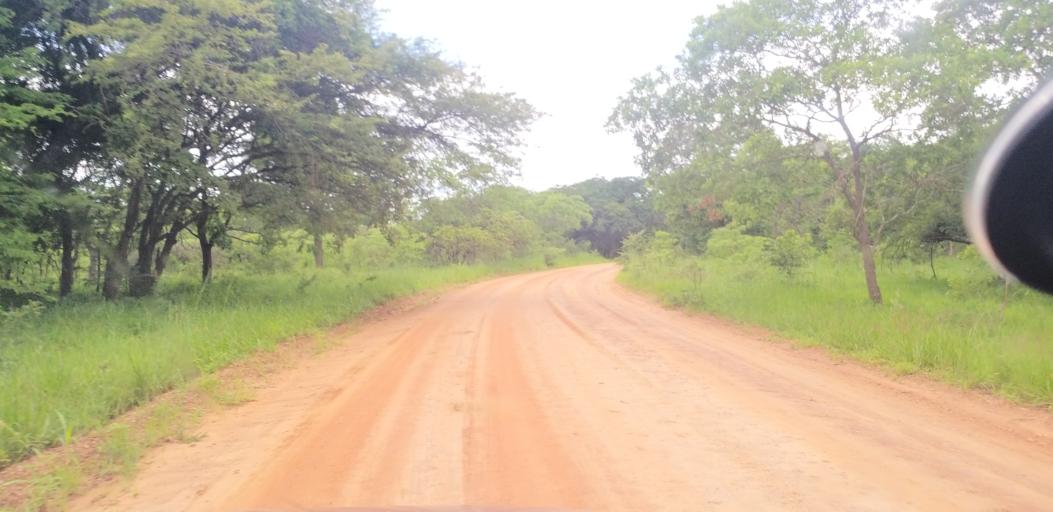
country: ZM
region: Lusaka
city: Chongwe
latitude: -15.1559
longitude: 28.4981
